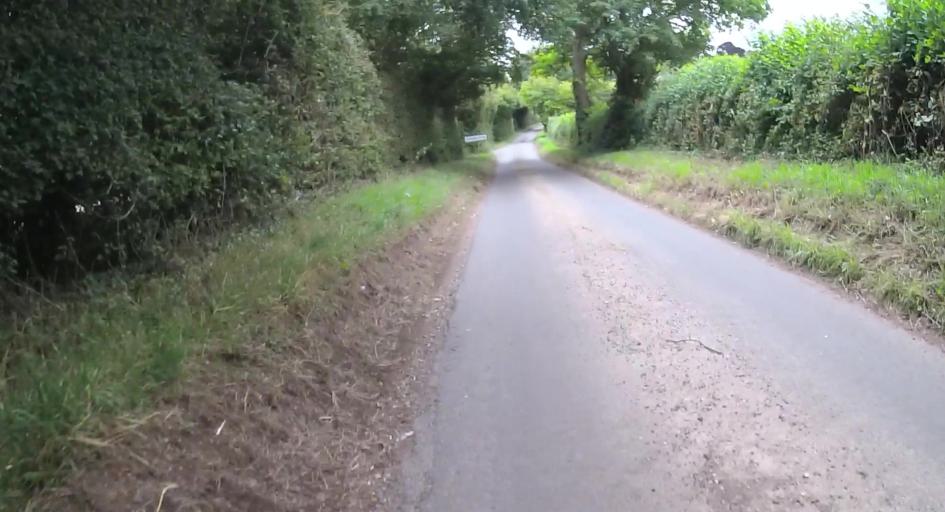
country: GB
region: England
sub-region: Hampshire
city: Four Marks
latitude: 51.0996
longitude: -1.1208
